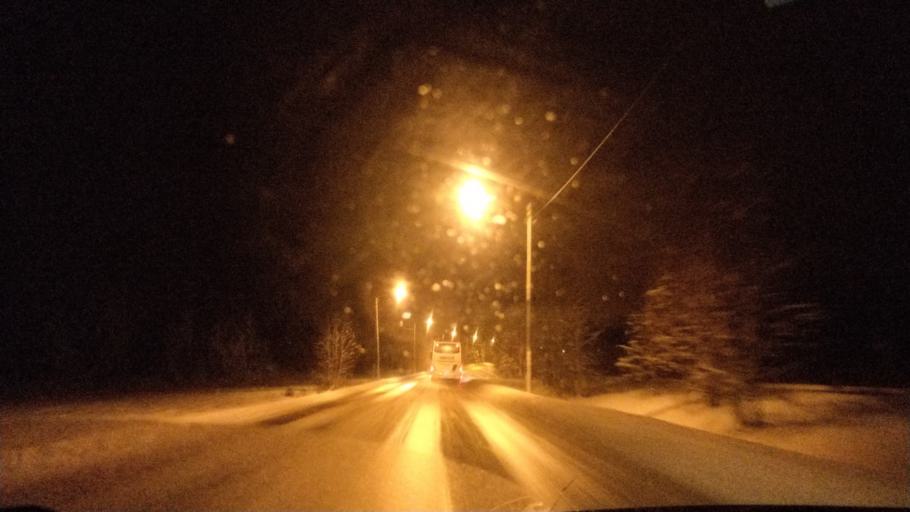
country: FI
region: Lapland
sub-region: Rovaniemi
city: Rovaniemi
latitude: 66.2925
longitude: 25.3503
